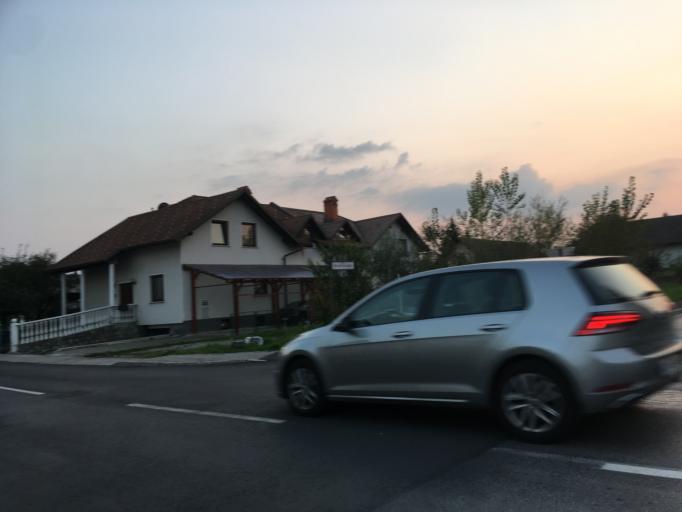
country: SI
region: Domzale
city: Vir
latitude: 46.1478
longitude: 14.6007
